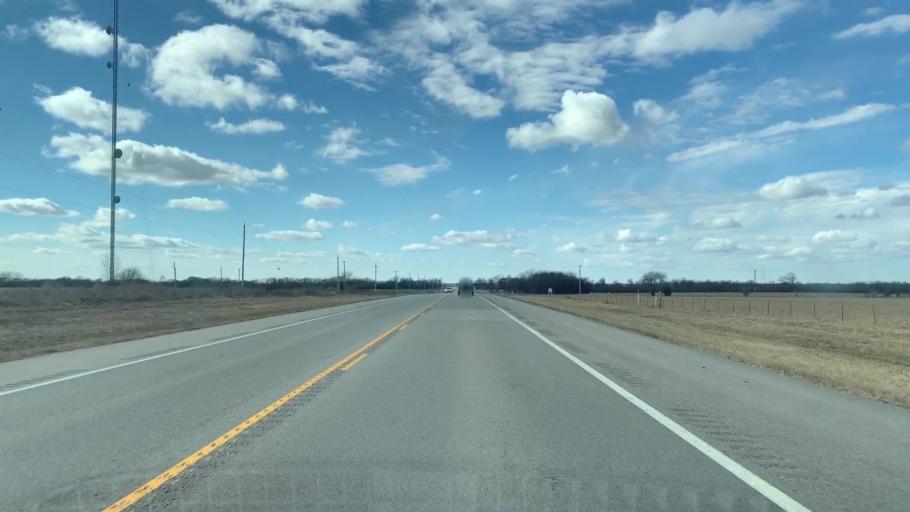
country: US
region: Kansas
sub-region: Labette County
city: Oswego
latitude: 37.3402
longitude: -95.0283
